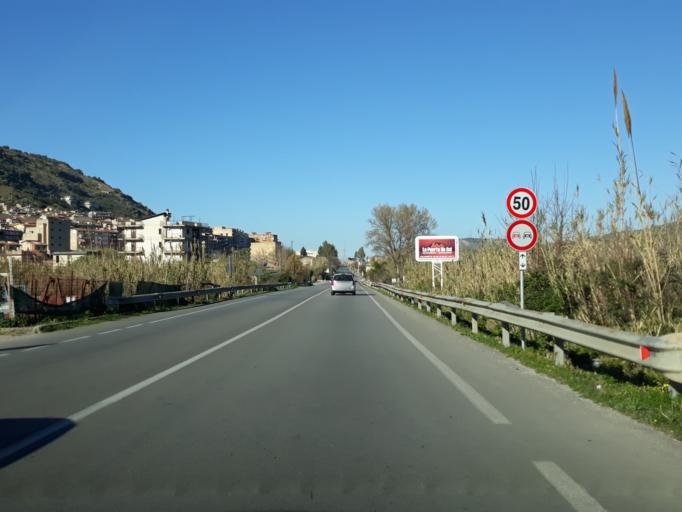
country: IT
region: Sicily
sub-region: Palermo
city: Misilmeri
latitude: 38.0296
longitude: 13.4561
